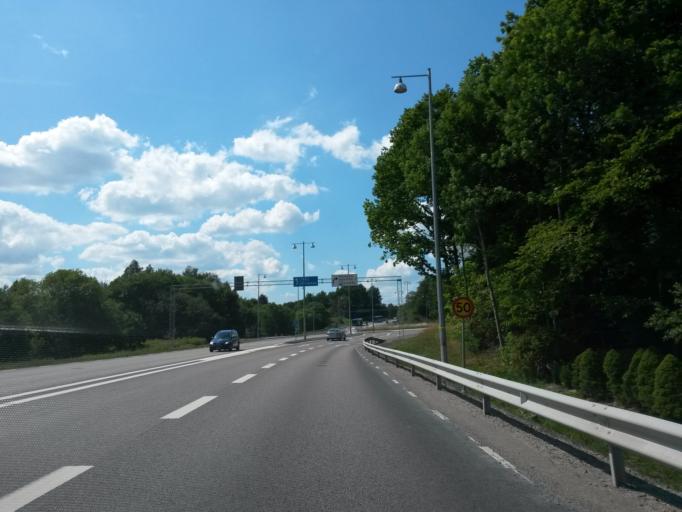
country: SE
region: Vaestra Goetaland
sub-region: Goteborg
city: Eriksbo
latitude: 57.7734
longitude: 12.0529
